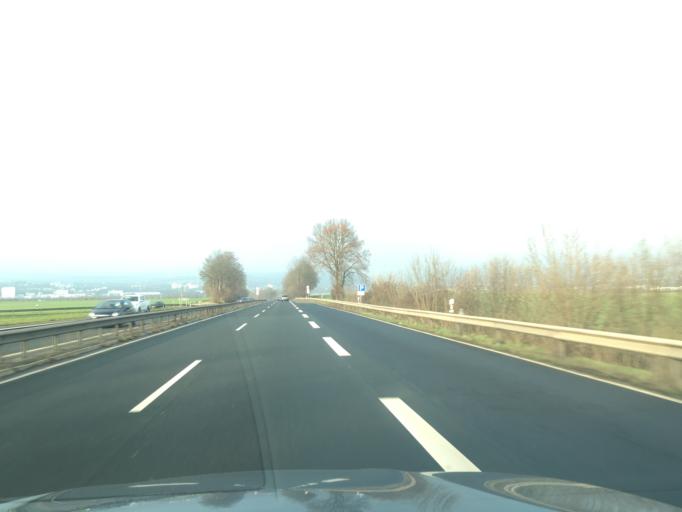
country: DE
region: Rheinland-Pfalz
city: Weissenthurm
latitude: 50.4126
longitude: 7.4394
